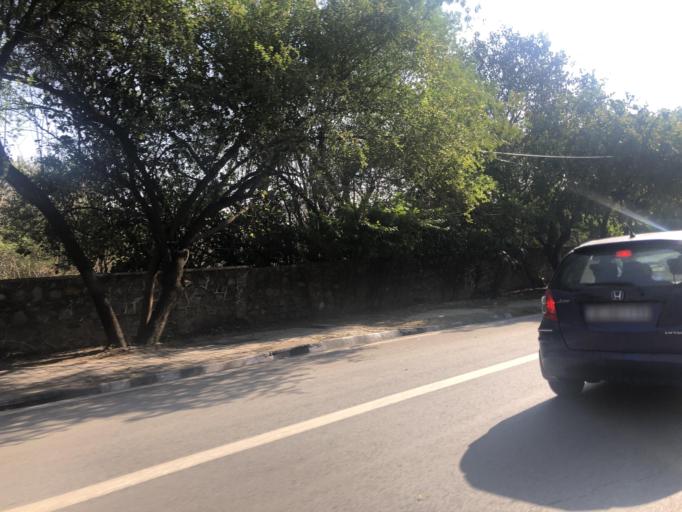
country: IN
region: NCT
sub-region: Central Delhi
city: Karol Bagh
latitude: 28.5486
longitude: 77.1629
